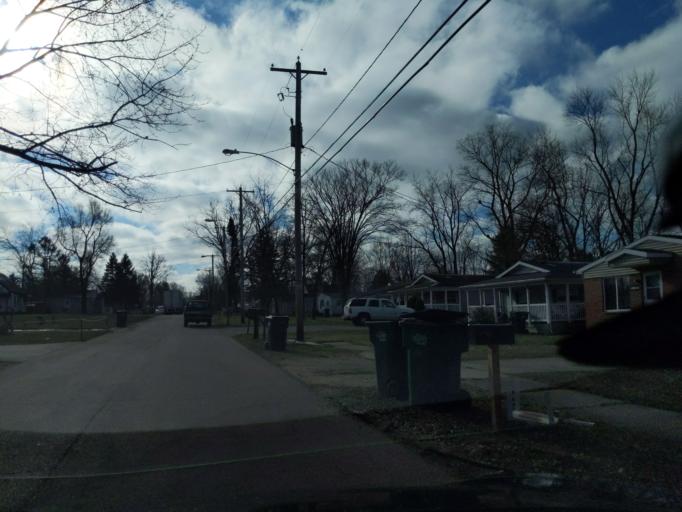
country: US
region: Michigan
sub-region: Ingham County
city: Lansing
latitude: 42.6868
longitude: -84.5771
